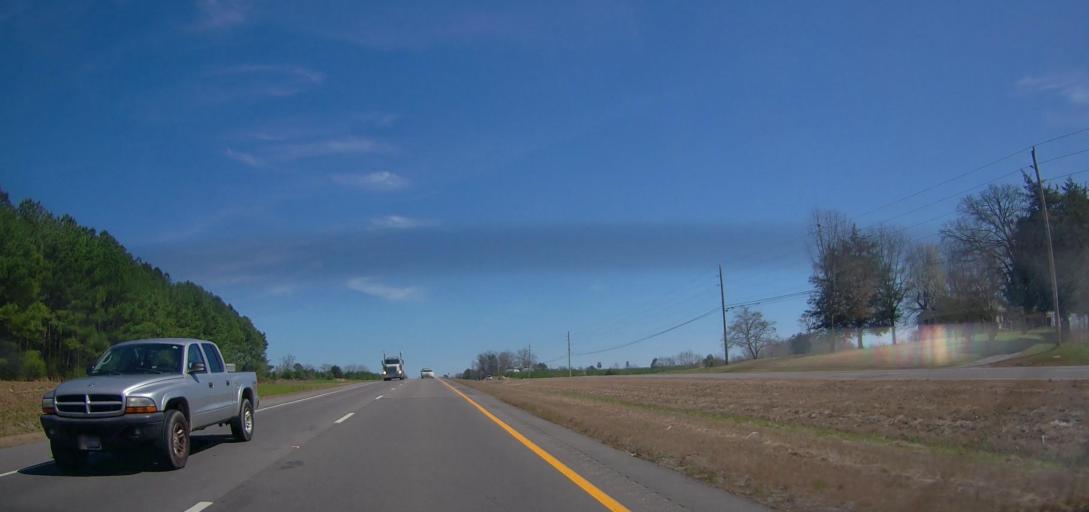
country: US
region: Alabama
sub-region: Cullman County
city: Cullman
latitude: 34.1813
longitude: -86.7625
